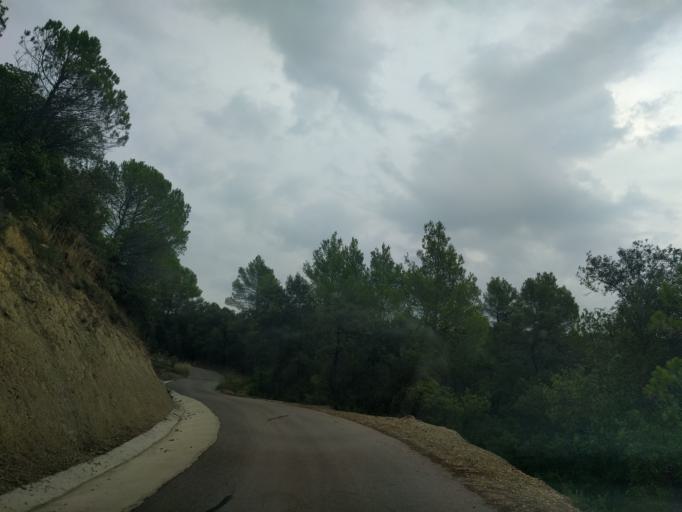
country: ES
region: Catalonia
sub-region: Provincia de Girona
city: la Cellera de Ter
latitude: 42.0149
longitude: 2.6328
